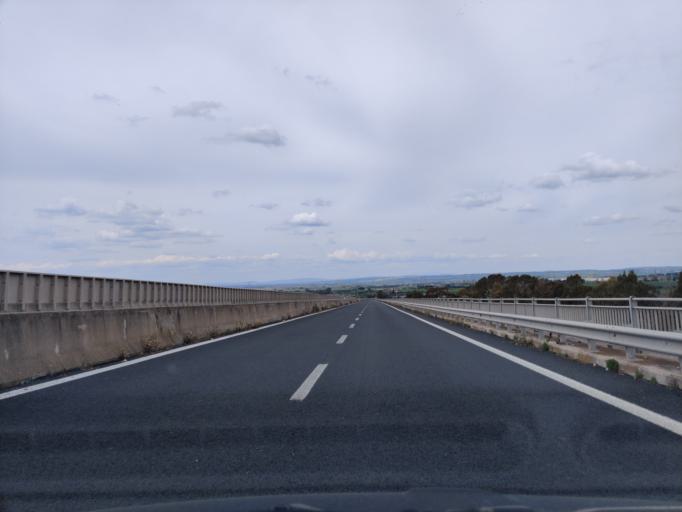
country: IT
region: Latium
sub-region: Citta metropolitana di Roma Capitale
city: Aurelia
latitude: 42.1401
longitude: 11.7941
